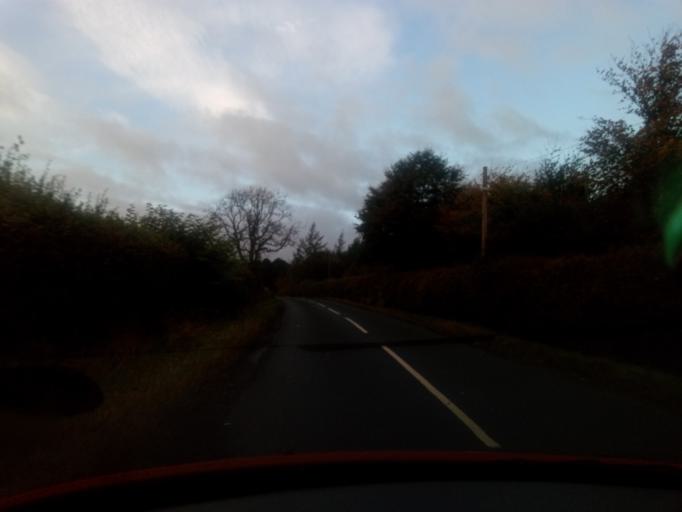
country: GB
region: Scotland
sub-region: The Scottish Borders
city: Jedburgh
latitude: 55.4410
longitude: -2.5918
